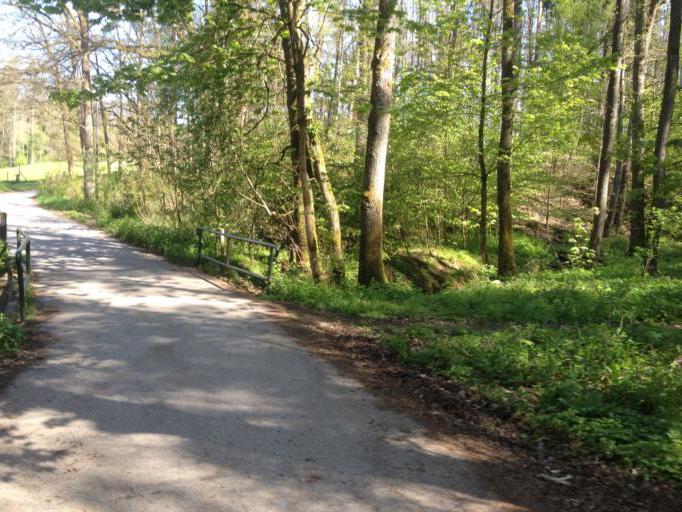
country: DE
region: Bavaria
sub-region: Regierungsbezirk Mittelfranken
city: Lauf an der Pegnitz
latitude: 49.5228
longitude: 11.2581
